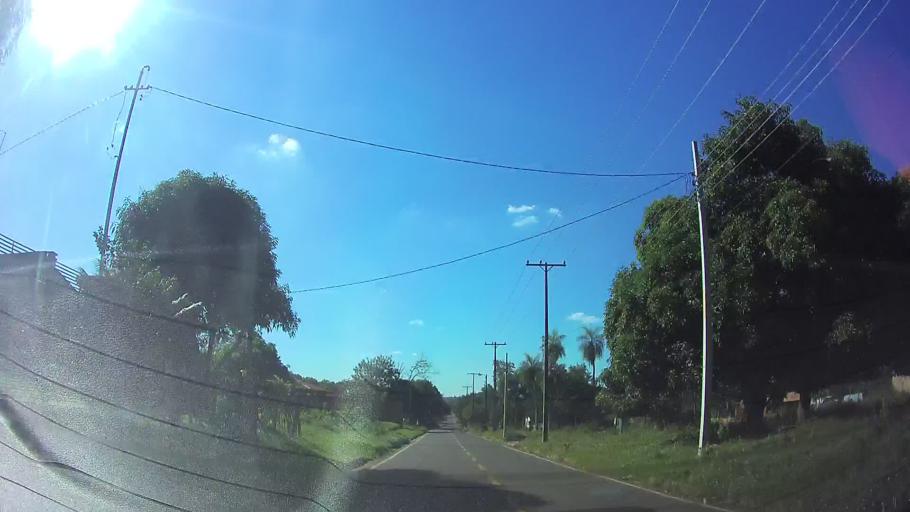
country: PY
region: Central
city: Limpio
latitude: -25.1999
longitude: -57.4783
